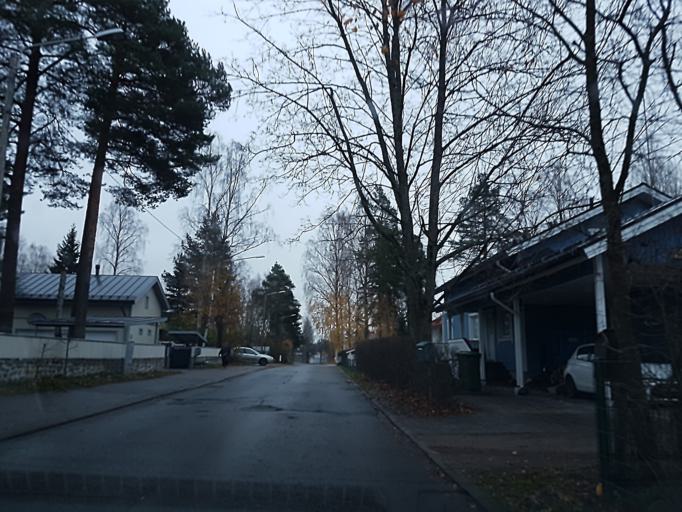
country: FI
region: Uusimaa
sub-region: Helsinki
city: Vantaa
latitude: 60.2403
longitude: 25.1016
